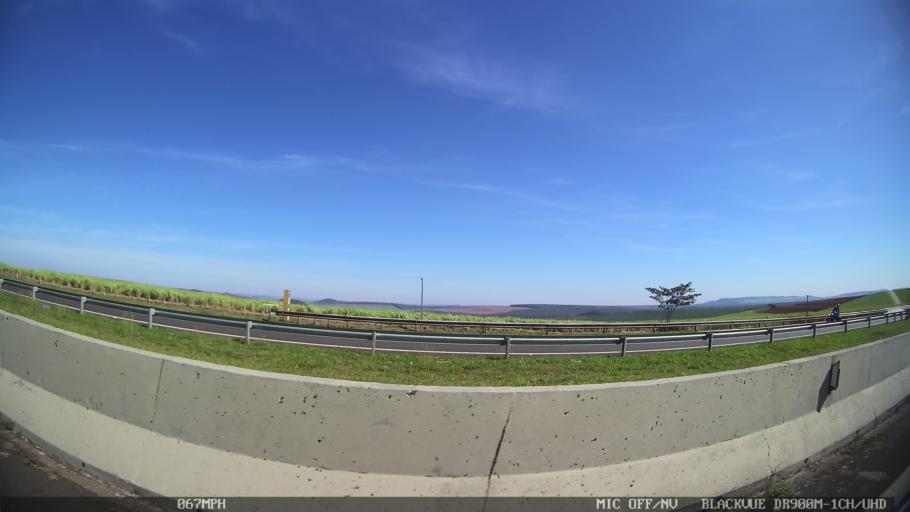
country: BR
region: Sao Paulo
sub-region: Santa Rita Do Passa Quatro
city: Santa Rita do Passa Quatro
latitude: -21.6665
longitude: -47.6077
